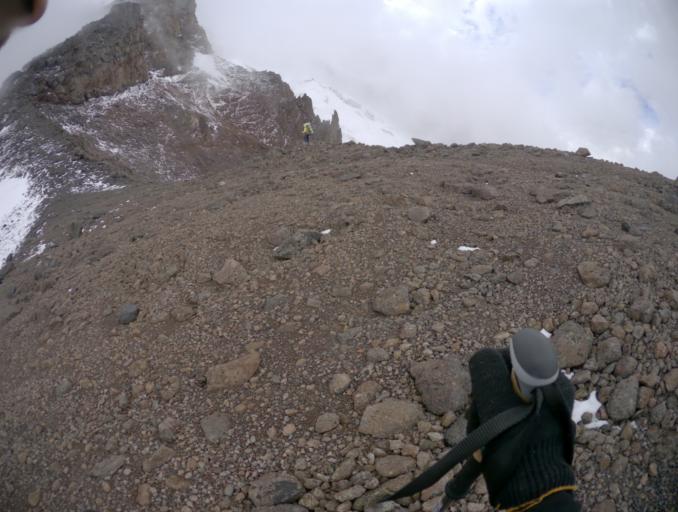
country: RU
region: Kabardino-Balkariya
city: Terskol
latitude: 43.3793
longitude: 42.4082
